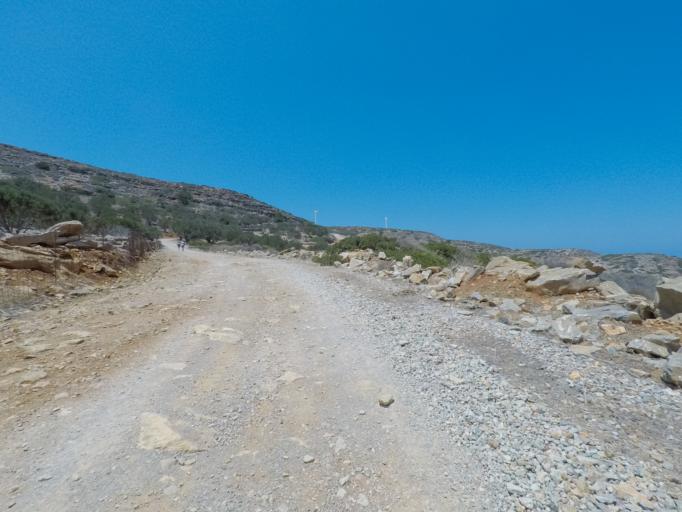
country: GR
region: Crete
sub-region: Nomos Lasithiou
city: Elounda
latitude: 35.3249
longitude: 25.7614
